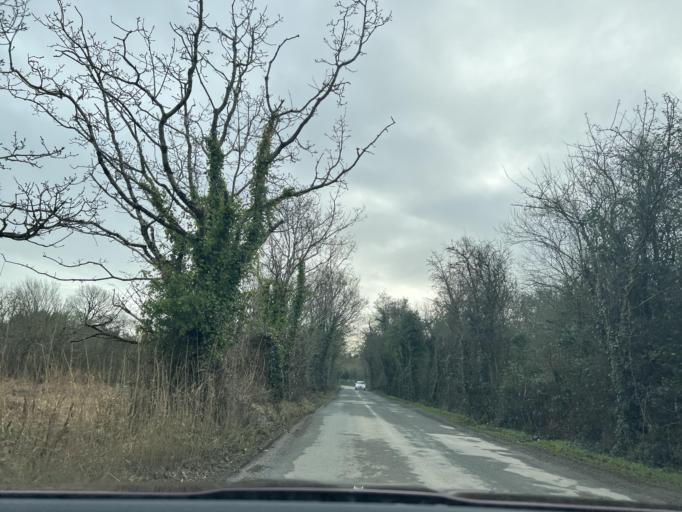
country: IE
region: Leinster
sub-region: Loch Garman
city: Castlebridge
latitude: 52.3845
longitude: -6.5653
